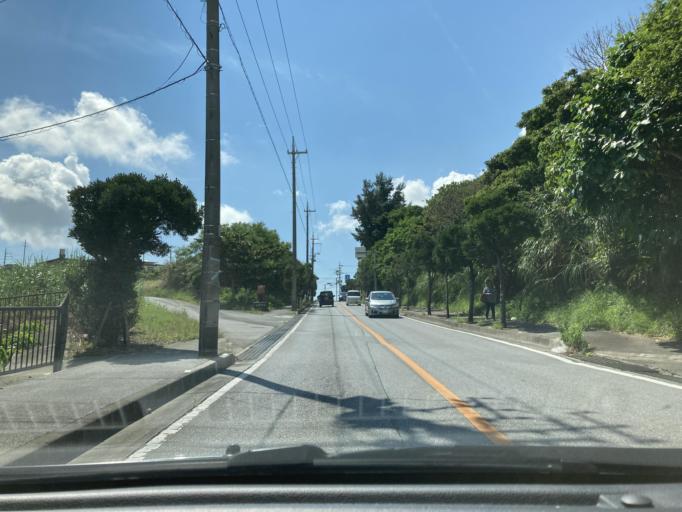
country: JP
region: Okinawa
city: Tomigusuku
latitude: 26.1675
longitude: 127.7545
